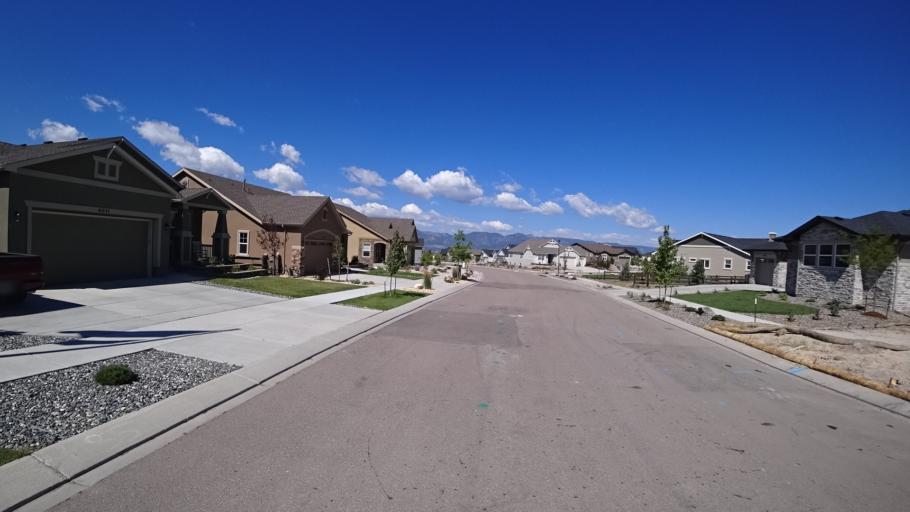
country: US
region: Colorado
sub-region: El Paso County
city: Black Forest
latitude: 38.9812
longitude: -104.7506
